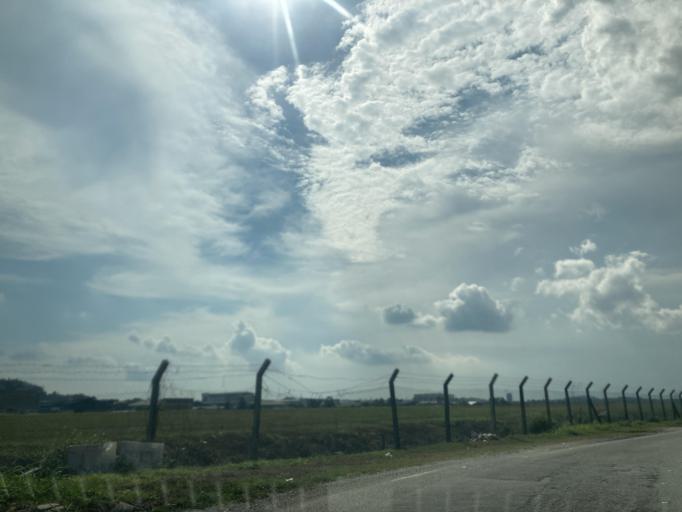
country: MY
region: Selangor
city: Kampung Baru Subang
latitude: 3.1393
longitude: 101.5475
